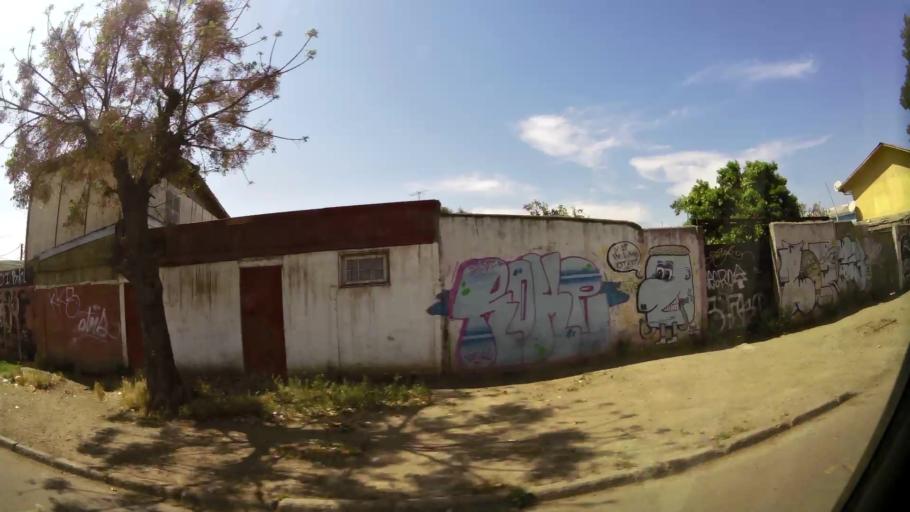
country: CL
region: Santiago Metropolitan
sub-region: Provincia de Santiago
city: Lo Prado
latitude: -33.4659
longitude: -70.7014
